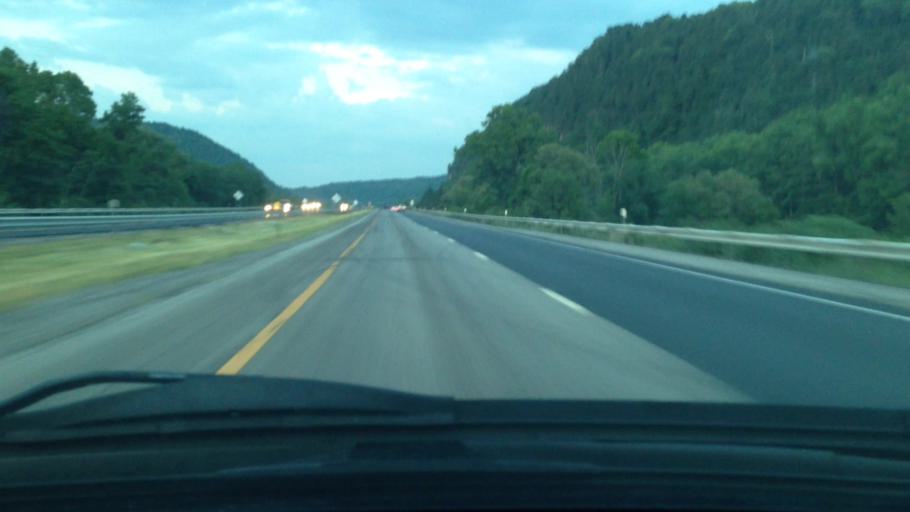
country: US
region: New York
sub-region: Montgomery County
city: Canajoharie
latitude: 42.8941
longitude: -74.4984
